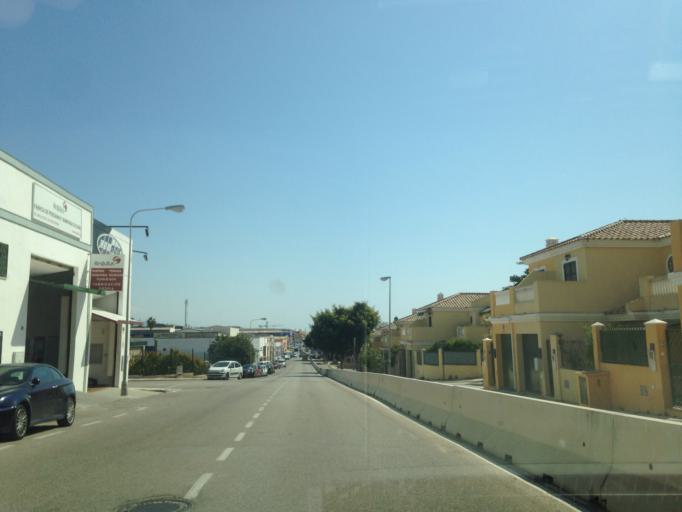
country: ES
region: Andalusia
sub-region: Provincia de Malaga
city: Malaga
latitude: 36.7013
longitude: -4.4760
